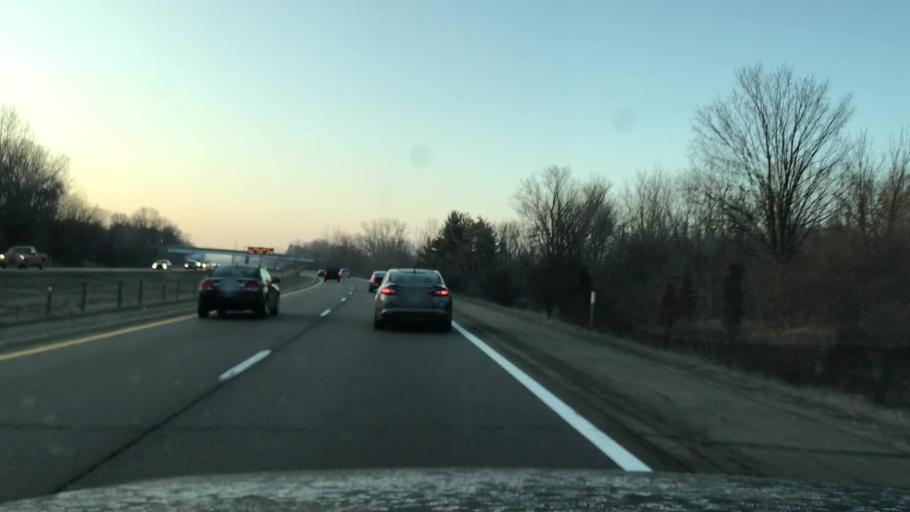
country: US
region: Michigan
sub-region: Kent County
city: East Grand Rapids
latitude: 42.9315
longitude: -85.5633
